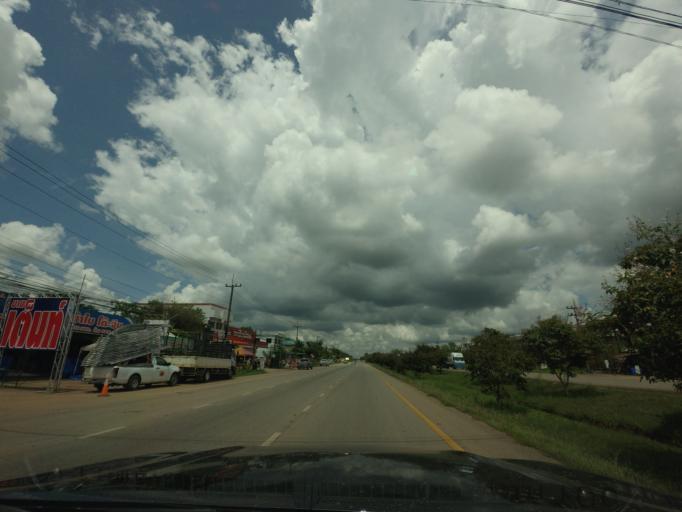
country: TH
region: Changwat Udon Thani
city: Udon Thani
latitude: 17.5330
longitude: 102.7998
